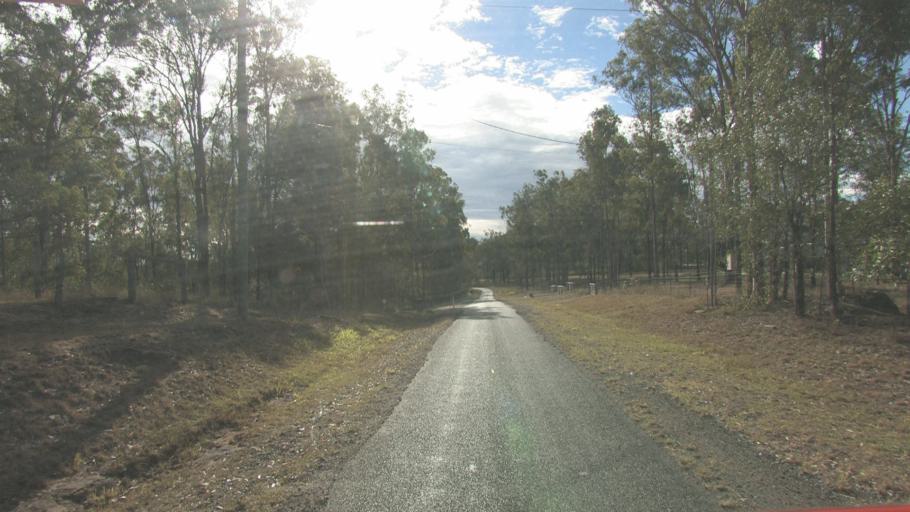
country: AU
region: Queensland
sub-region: Logan
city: Cedar Vale
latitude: -27.8414
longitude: 153.0682
